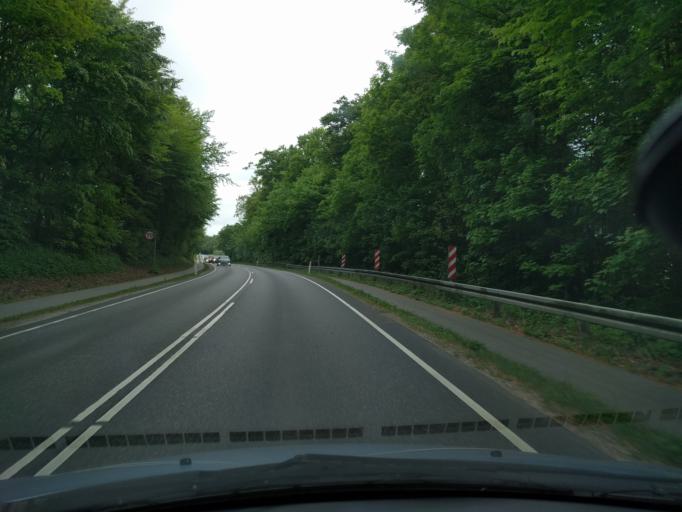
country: DK
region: Zealand
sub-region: Naestved Kommune
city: Naestved
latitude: 55.1917
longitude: 11.8481
